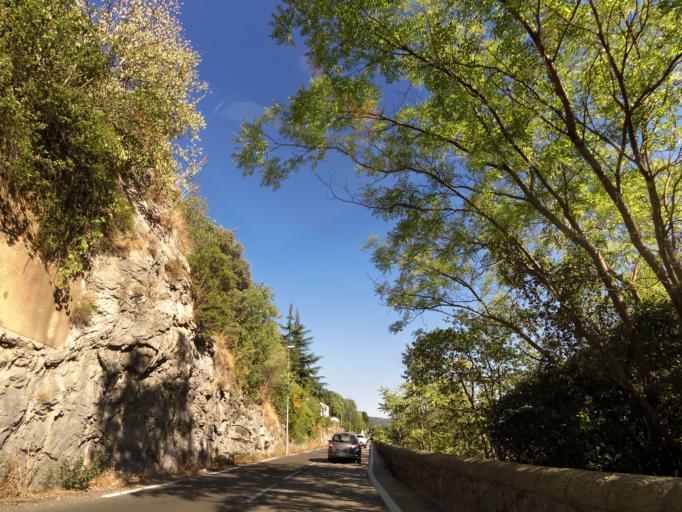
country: FR
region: Languedoc-Roussillon
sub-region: Departement de l'Herault
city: Ganges
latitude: 43.9373
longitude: 3.6953
